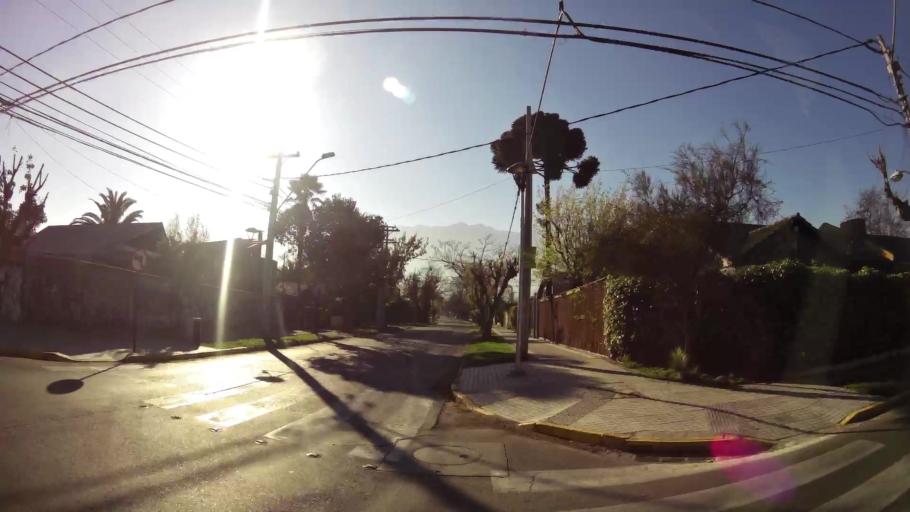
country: CL
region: Santiago Metropolitan
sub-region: Provincia de Santiago
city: Villa Presidente Frei, Nunoa, Santiago, Chile
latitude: -33.4593
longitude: -70.5648
